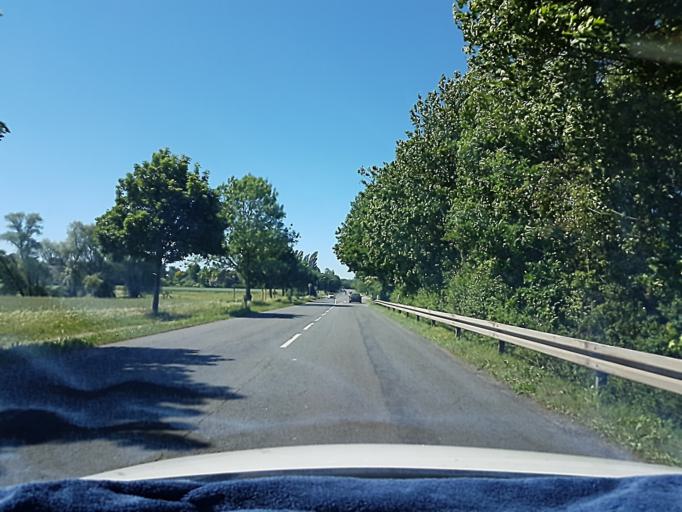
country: DE
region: North Rhine-Westphalia
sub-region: Regierungsbezirk Dusseldorf
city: Ratingen
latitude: 51.3579
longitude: 6.8596
